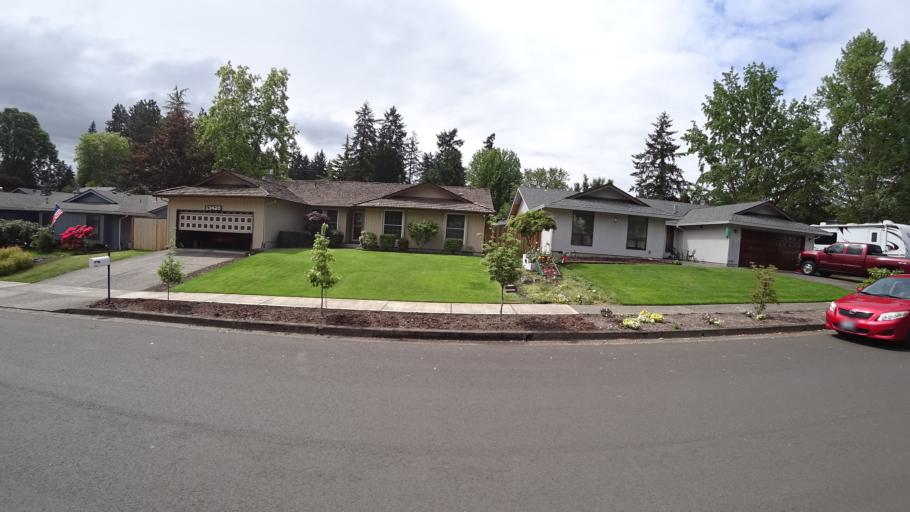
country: US
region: Oregon
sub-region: Washington County
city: Beaverton
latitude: 45.4702
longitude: -122.8148
